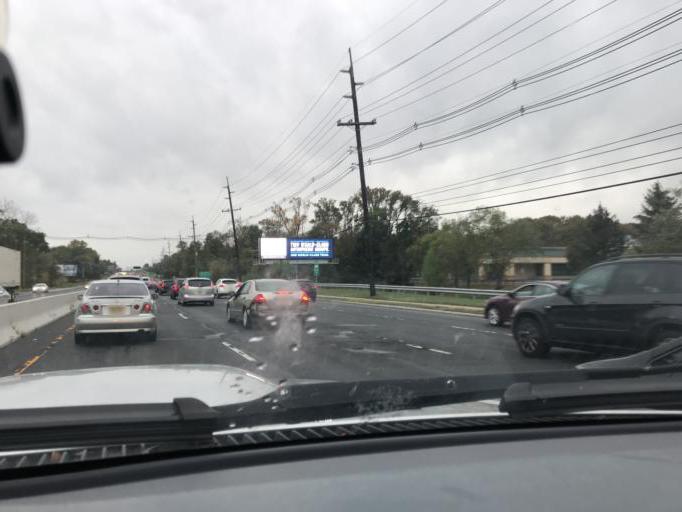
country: US
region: New Jersey
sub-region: Mercer County
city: Princeton
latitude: 40.3081
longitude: -74.6664
